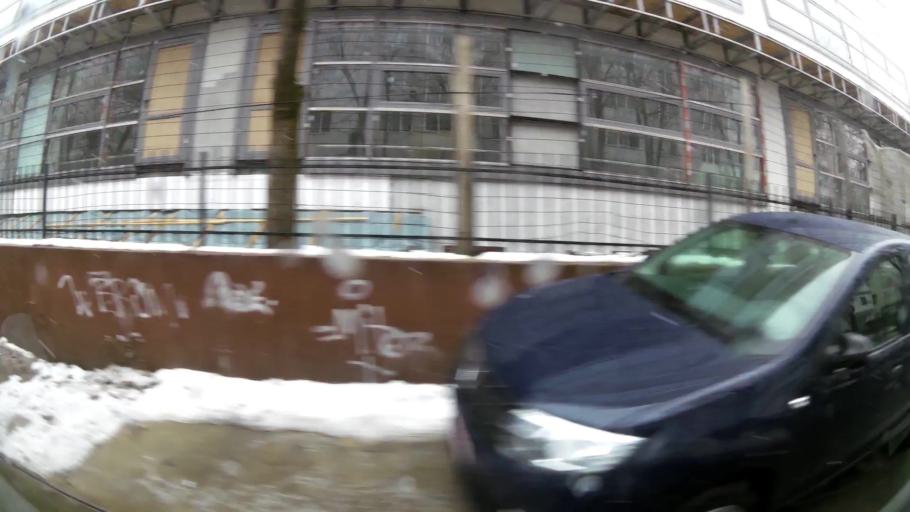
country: RO
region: Ilfov
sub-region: Comuna Chiajna
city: Rosu
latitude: 44.4805
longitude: 26.0504
